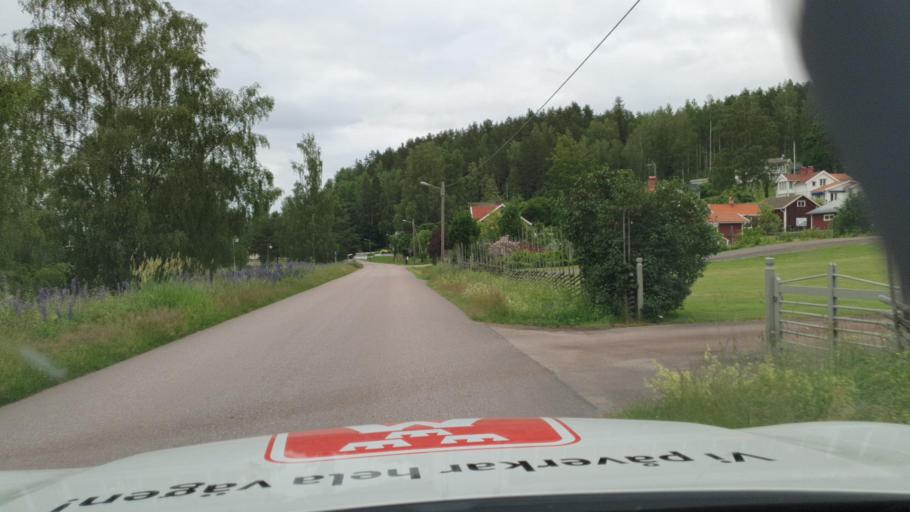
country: SE
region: Vaermland
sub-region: Kils Kommun
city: Kil
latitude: 59.5228
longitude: 13.3312
